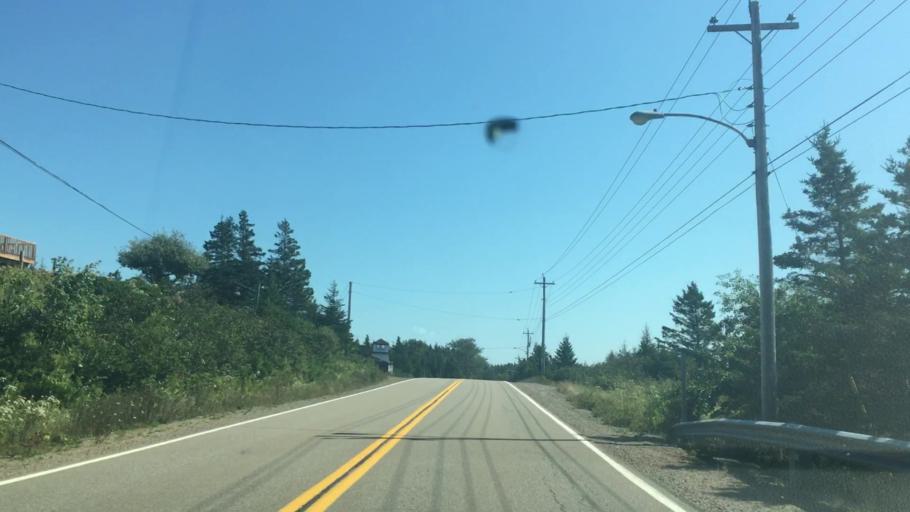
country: CA
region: Nova Scotia
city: Antigonish
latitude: 45.0223
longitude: -62.0137
